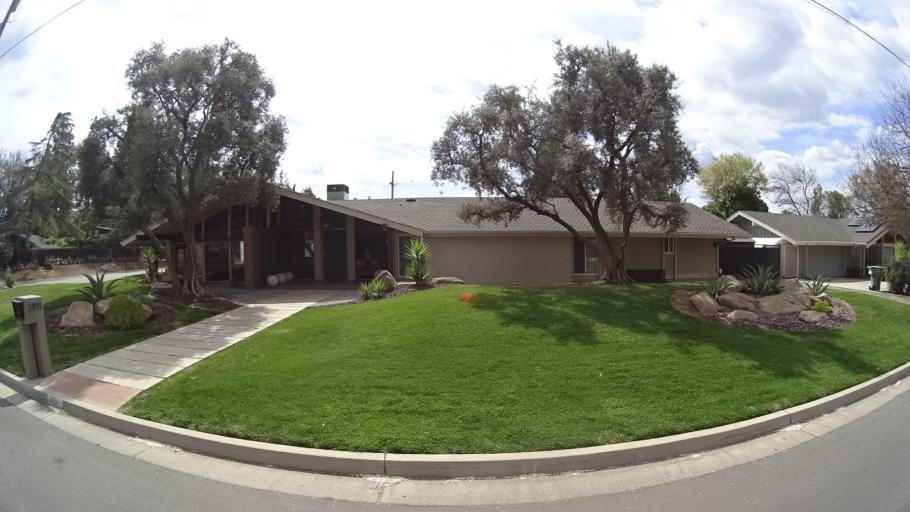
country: US
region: California
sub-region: Fresno County
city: Fresno
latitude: 36.8191
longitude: -119.8376
